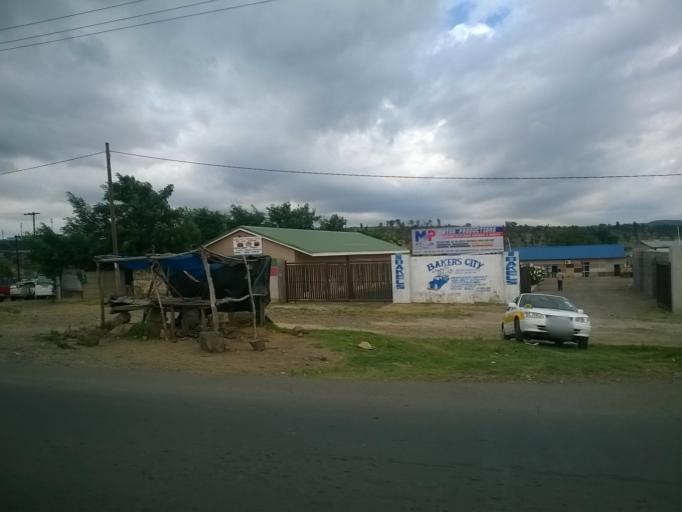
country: LS
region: Maseru
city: Maseru
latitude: -29.3046
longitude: 27.5158
